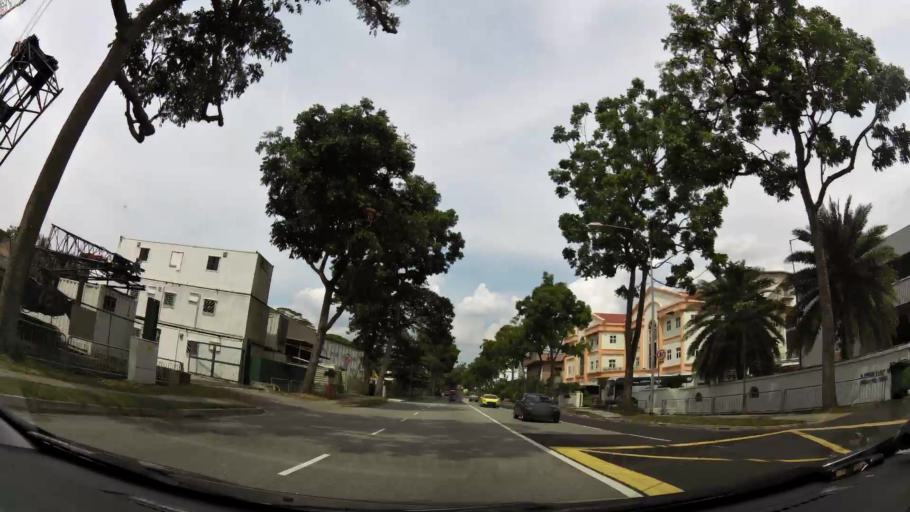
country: MY
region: Johor
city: Johor Bahru
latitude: 1.4039
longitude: 103.7548
